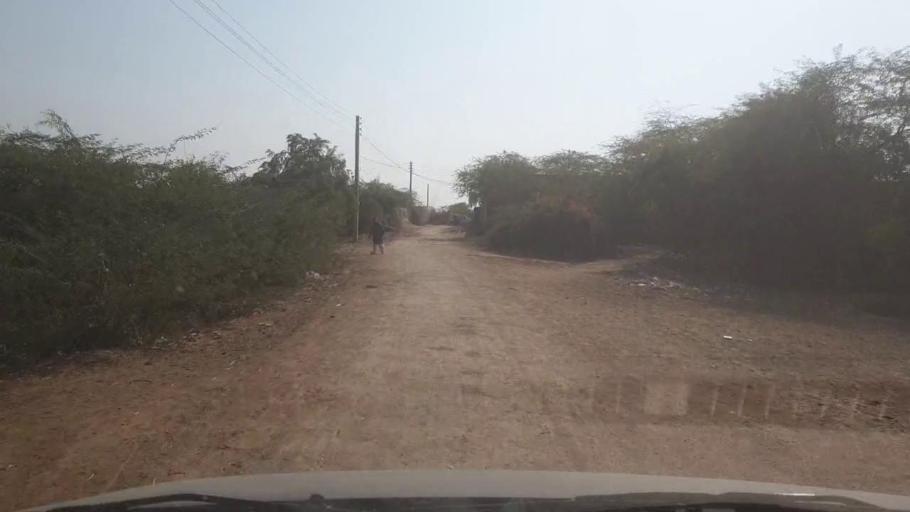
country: PK
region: Sindh
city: Samaro
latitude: 25.1830
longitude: 69.3667
